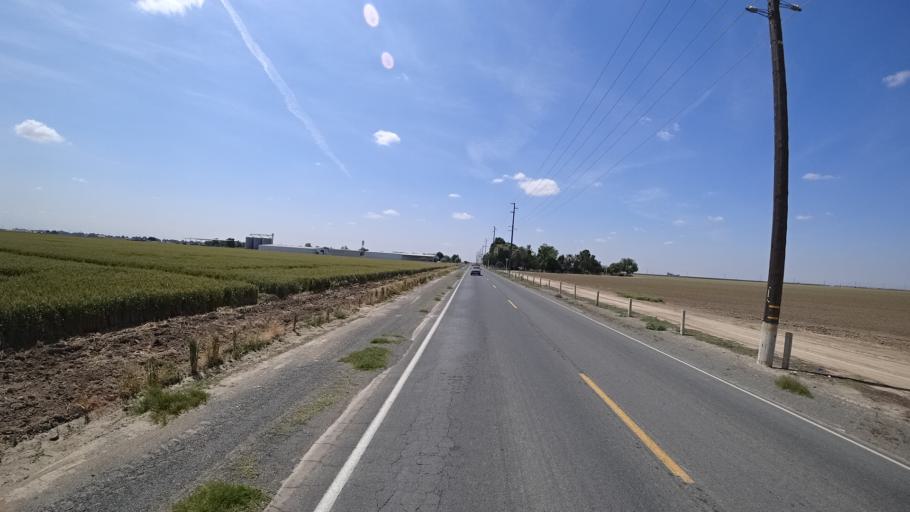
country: US
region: California
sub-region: Tulare County
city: Goshen
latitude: 36.3042
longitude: -119.4925
